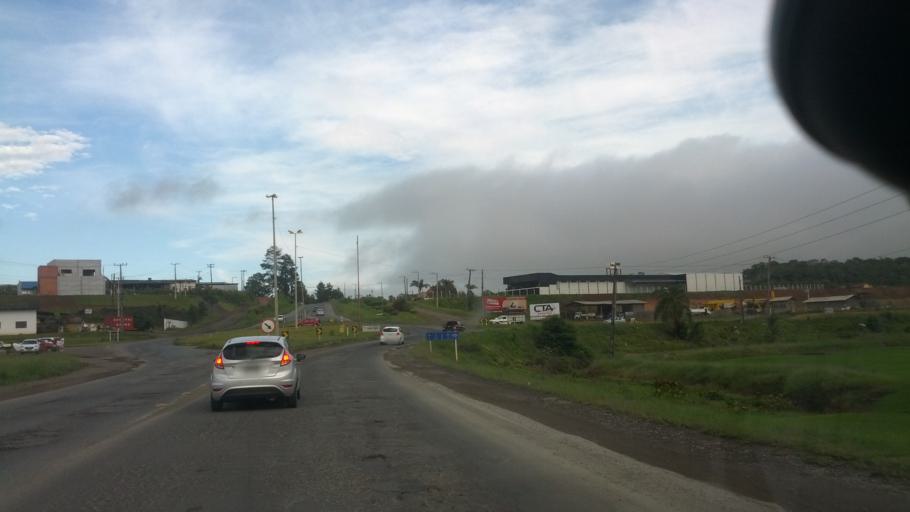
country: BR
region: Santa Catarina
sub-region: Otacilio Costa
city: Otacilio Costa
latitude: -27.2515
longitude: -49.9587
